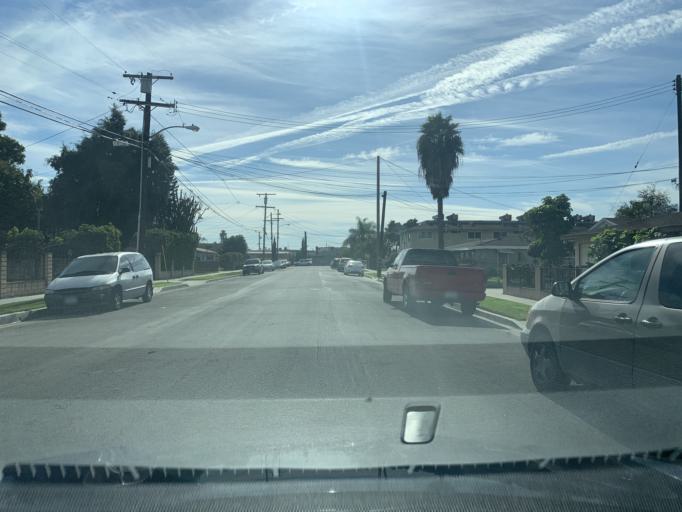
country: US
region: California
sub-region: Los Angeles County
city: South El Monte
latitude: 34.0576
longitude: -118.0586
